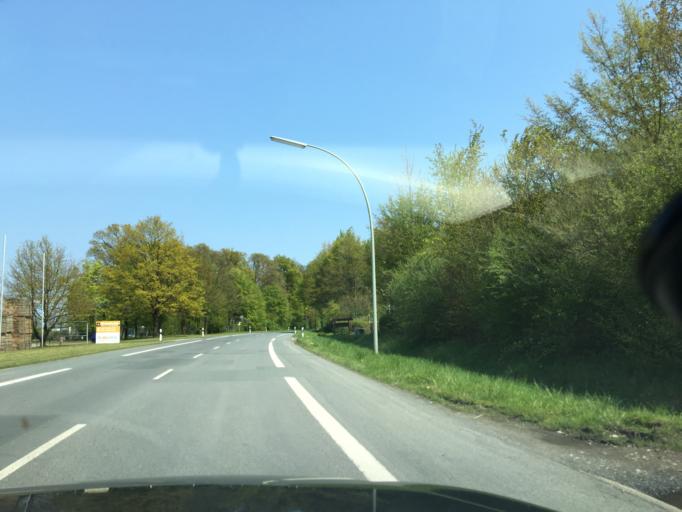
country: DE
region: North Rhine-Westphalia
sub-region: Regierungsbezirk Munster
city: Senden
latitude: 51.8461
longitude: 7.4740
